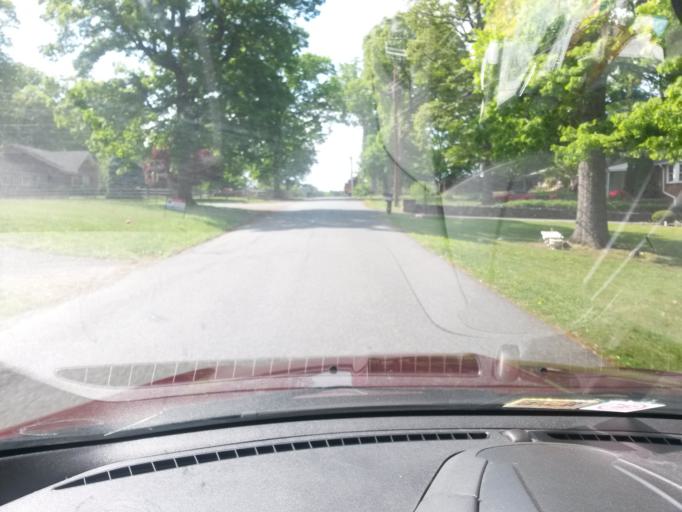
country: US
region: Virginia
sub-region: Campbell County
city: Timberlake
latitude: 37.3531
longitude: -79.2211
